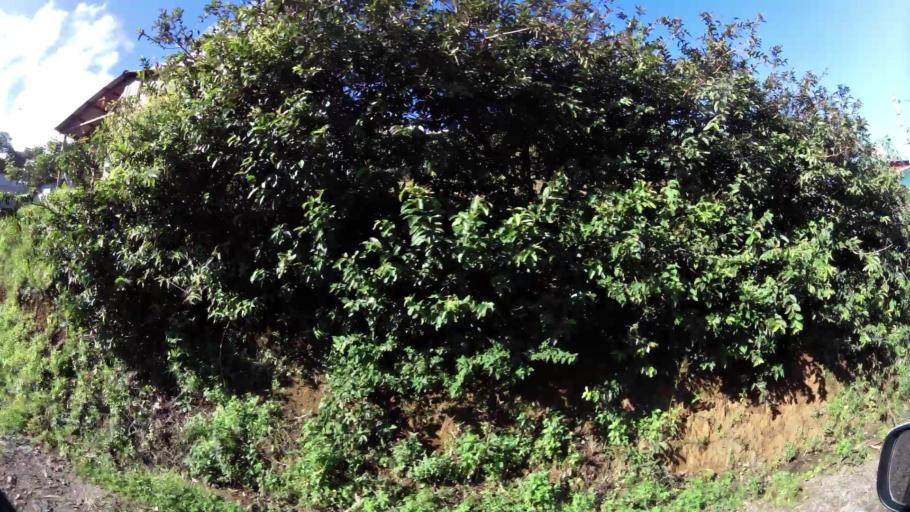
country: CR
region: Guanacaste
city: Juntas
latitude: 10.3153
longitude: -84.8327
